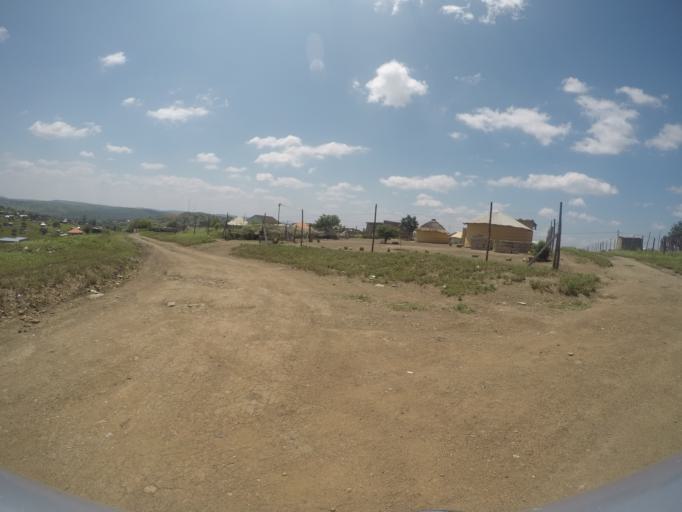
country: ZA
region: KwaZulu-Natal
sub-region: uThungulu District Municipality
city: Empangeni
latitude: -28.6086
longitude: 31.7376
